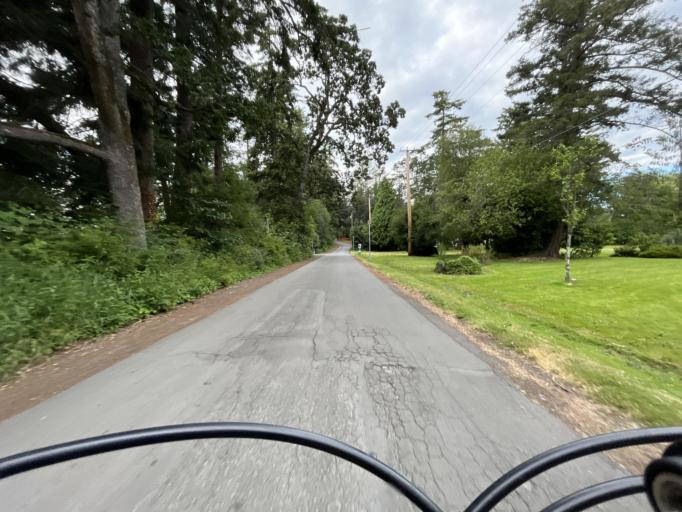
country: CA
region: British Columbia
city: Oak Bay
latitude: 48.4800
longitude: -123.3456
